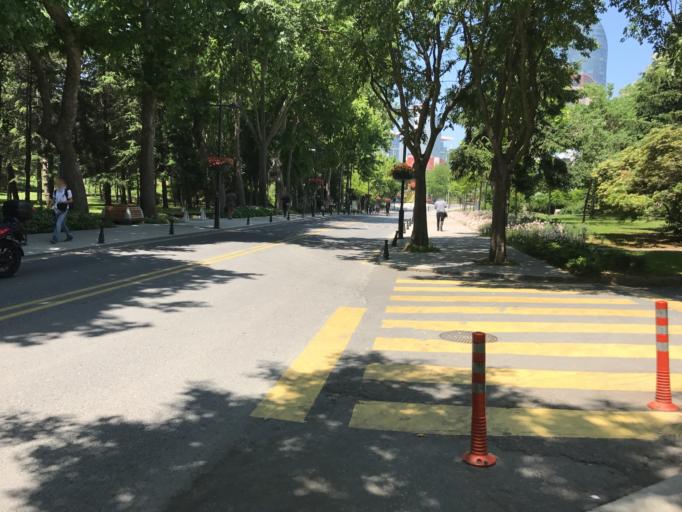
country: TR
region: Istanbul
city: Sisli
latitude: 41.1056
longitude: 29.0226
